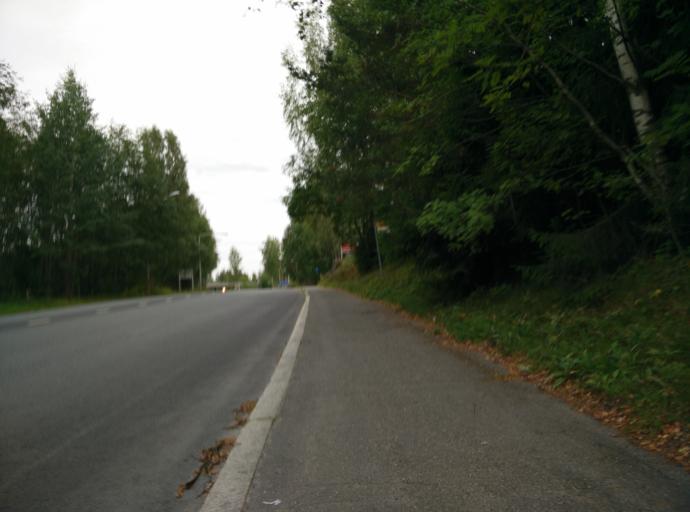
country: FI
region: Haeme
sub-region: Haemeenlinna
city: Haemeenlinna
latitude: 60.9837
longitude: 24.5019
